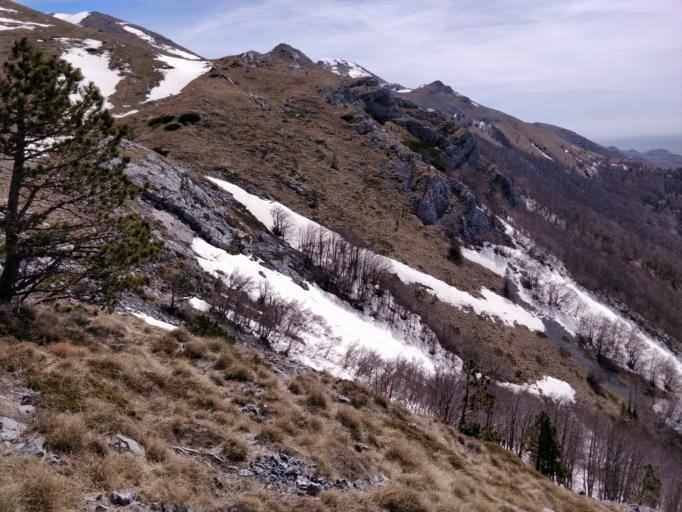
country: HR
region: Zadarska
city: Starigrad
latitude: 44.3390
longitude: 15.5415
